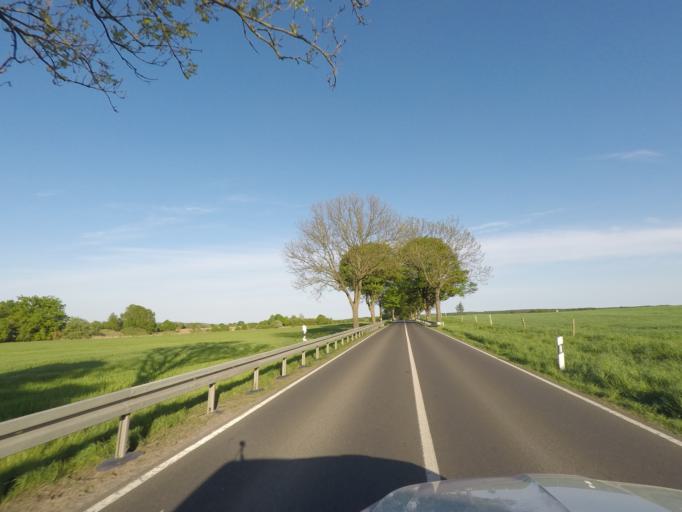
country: DE
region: Brandenburg
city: Hohenfinow
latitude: 52.8083
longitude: 13.9293
